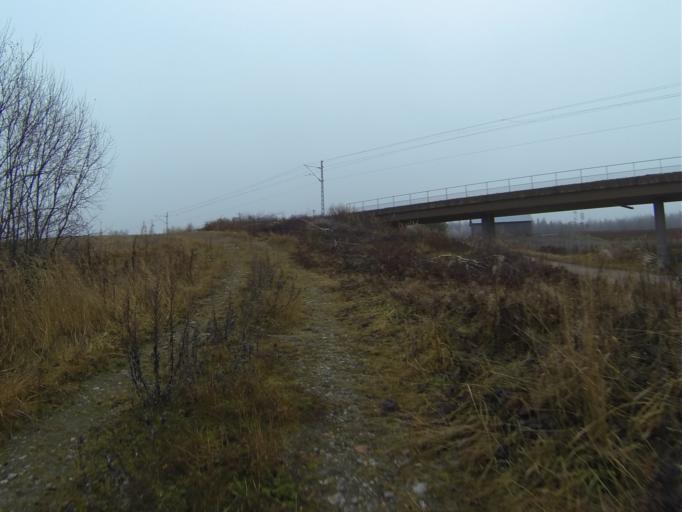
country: FI
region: Varsinais-Suomi
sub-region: Salo
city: Halikko
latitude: 60.4119
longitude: 22.9491
